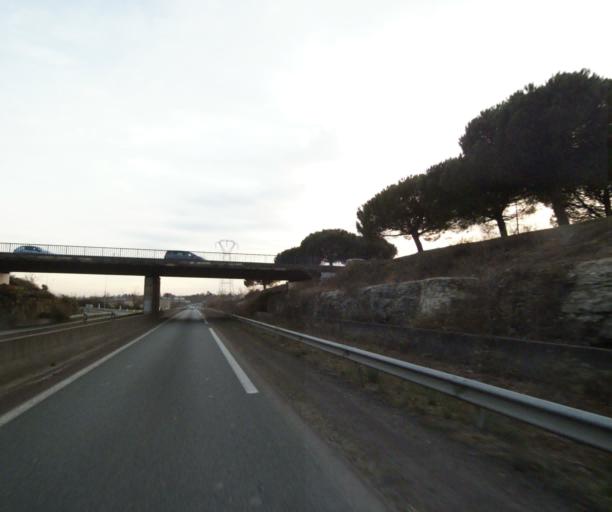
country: FR
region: Poitou-Charentes
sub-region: Departement de la Charente-Maritime
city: Fontcouverte
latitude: 45.7462
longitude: -0.6001
